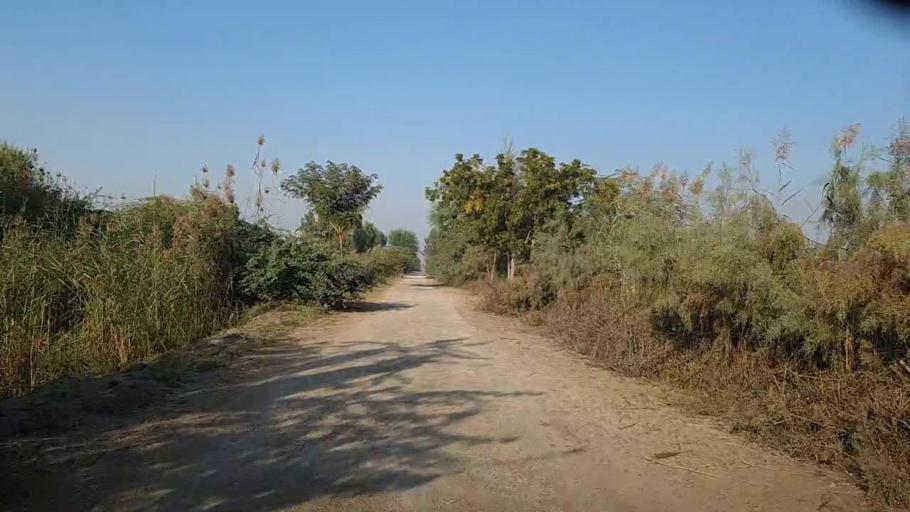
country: PK
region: Sindh
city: Ranipur
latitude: 27.2478
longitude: 68.5055
